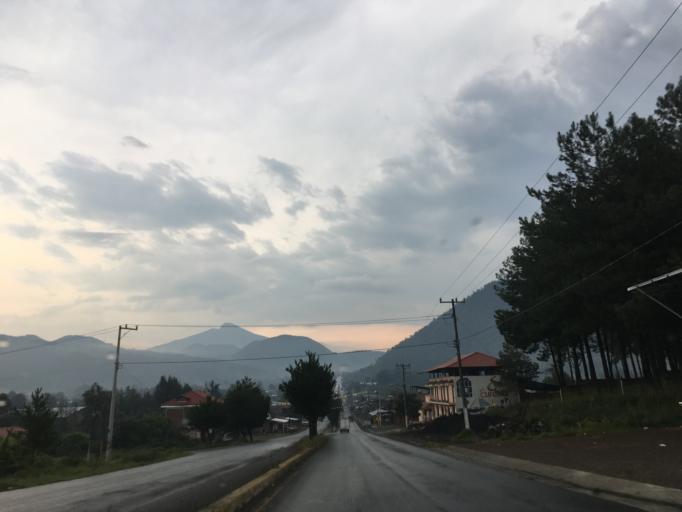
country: MX
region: Michoacan
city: Capacuaro
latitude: 19.5207
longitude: -102.1107
